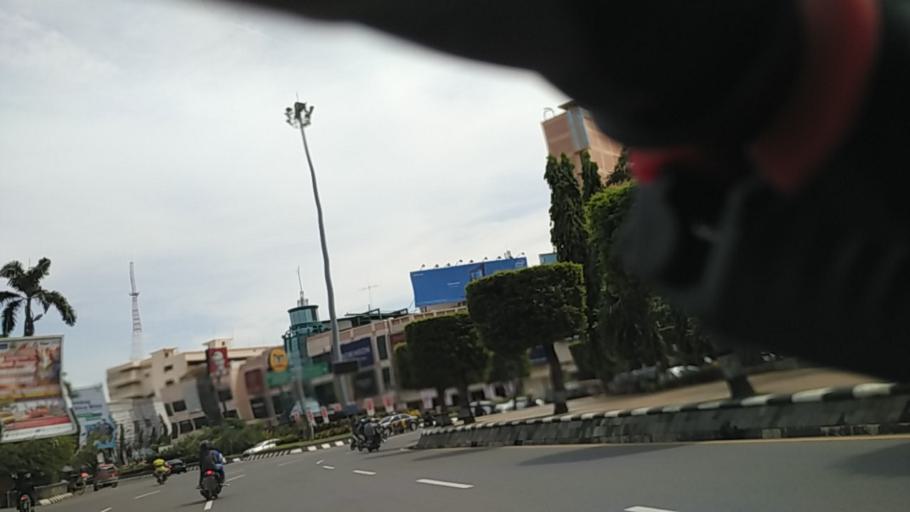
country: ID
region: Central Java
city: Semarang
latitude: -6.9896
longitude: 110.4225
